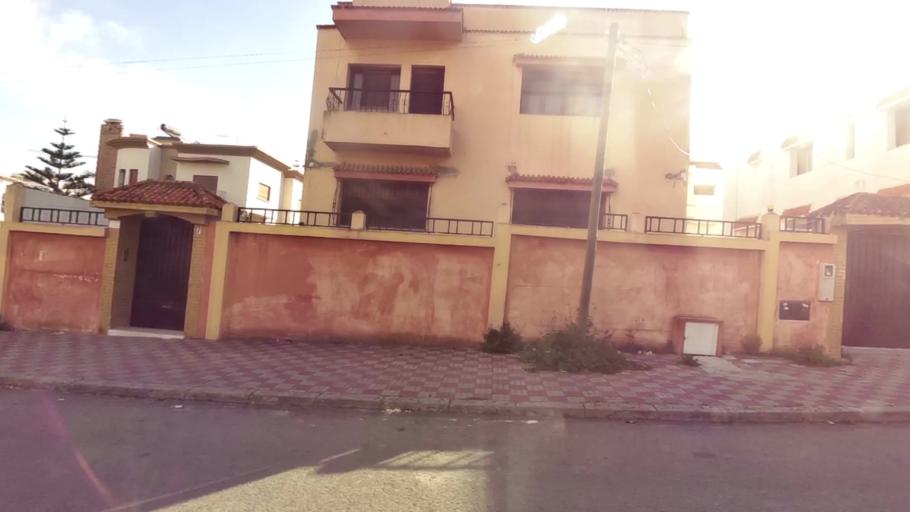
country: MA
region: Tanger-Tetouan
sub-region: Tanger-Assilah
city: Tangier
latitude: 35.7698
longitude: -5.7993
